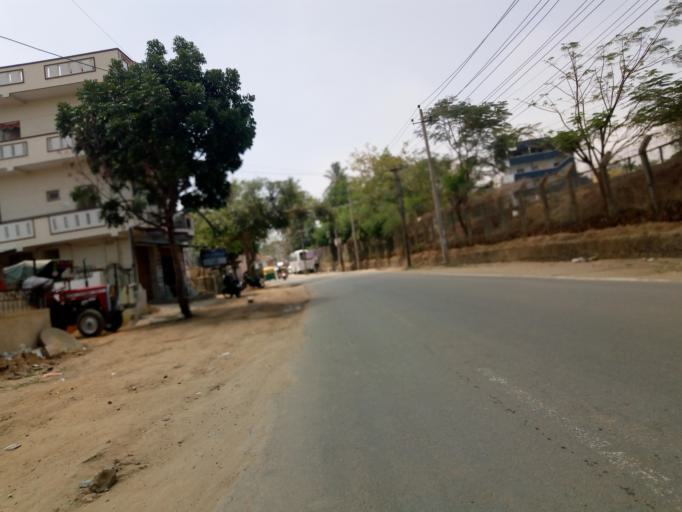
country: IN
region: Karnataka
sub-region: Bangalore Urban
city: Bangalore
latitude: 12.8915
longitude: 77.6559
